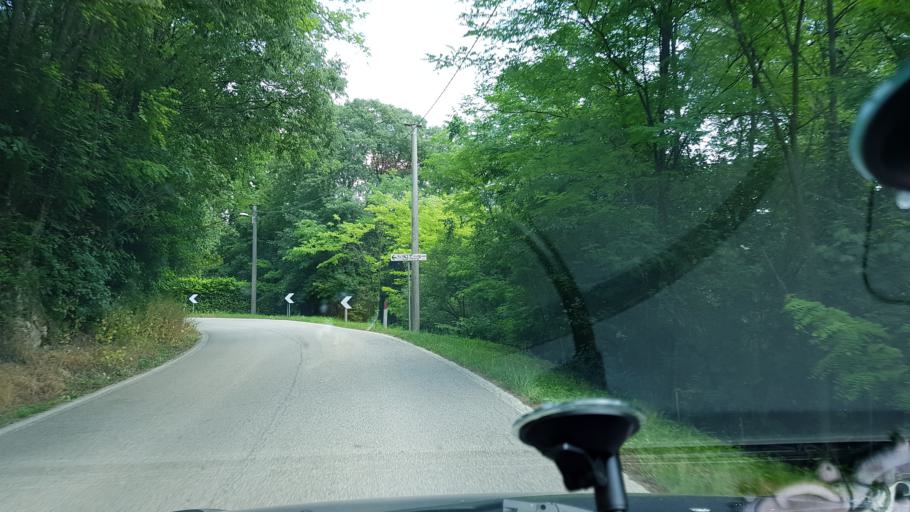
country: IT
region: Friuli Venezia Giulia
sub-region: Provincia di Gorizia
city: Savogna d'Isonzo
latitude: 45.8936
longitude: 13.5730
